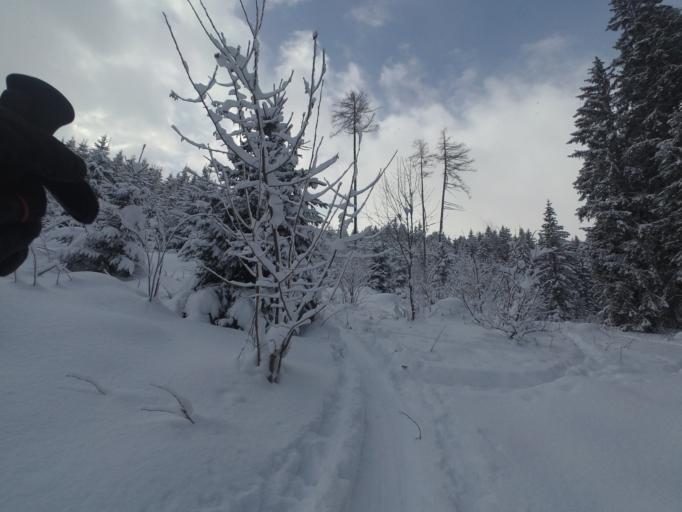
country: AT
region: Salzburg
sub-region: Politischer Bezirk Zell am See
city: Lend
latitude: 47.3092
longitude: 13.0621
